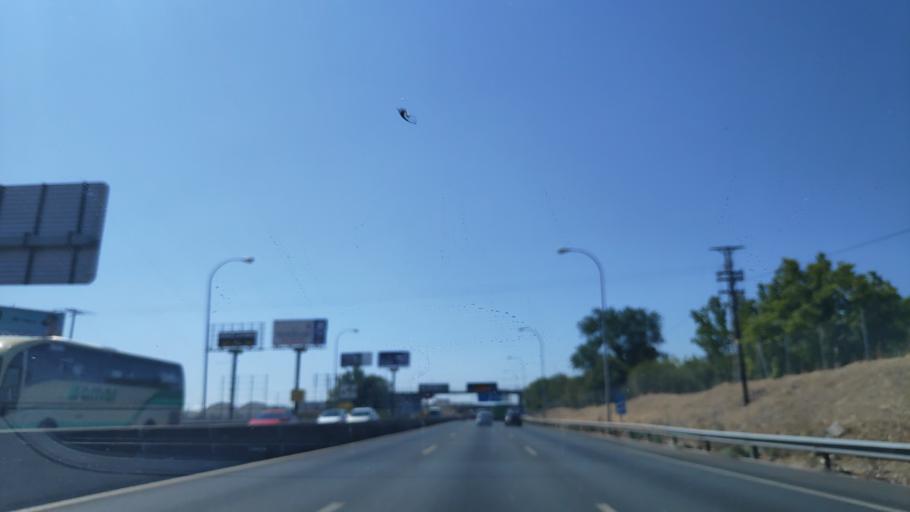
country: ES
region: Madrid
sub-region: Provincia de Madrid
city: Getafe
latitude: 40.2888
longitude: -3.7423
